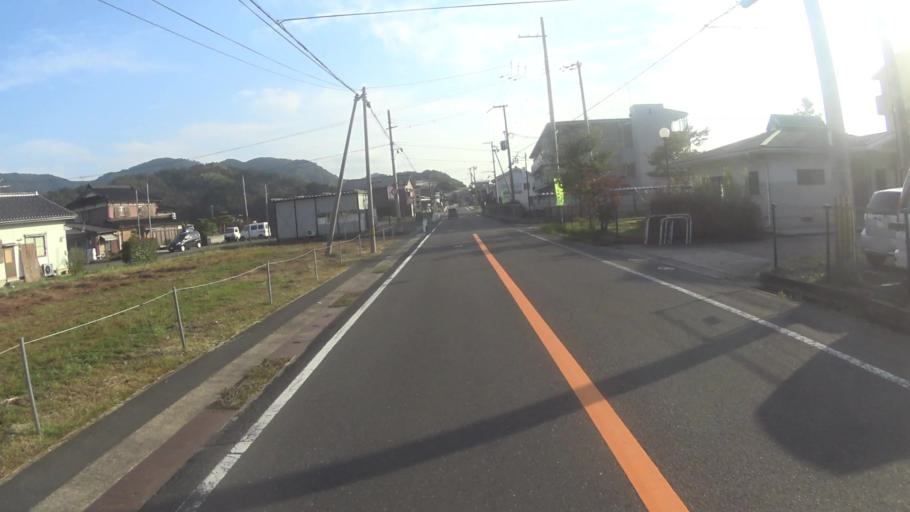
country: JP
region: Kyoto
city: Miyazu
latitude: 35.6538
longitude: 135.0924
